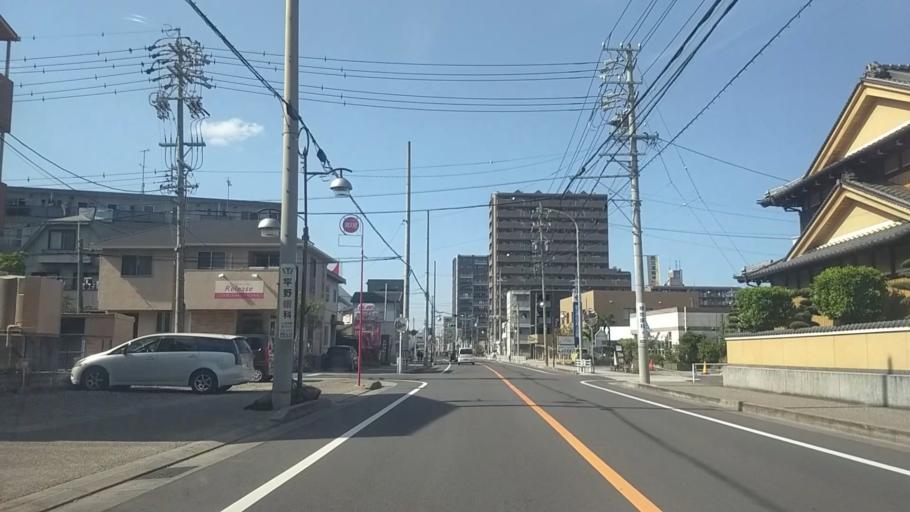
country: JP
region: Aichi
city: Anjo
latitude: 34.9831
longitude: 137.0844
